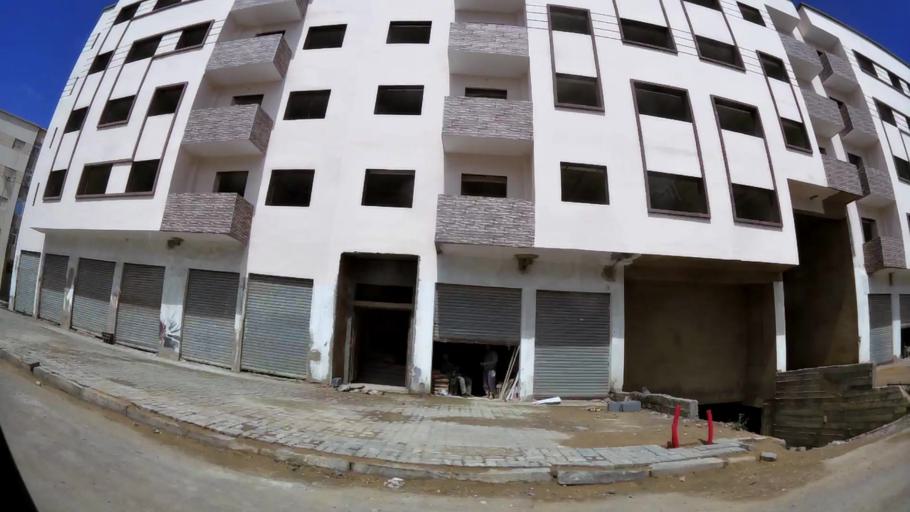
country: MA
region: Grand Casablanca
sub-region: Mediouna
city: Tit Mellil
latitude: 33.6090
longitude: -7.4817
